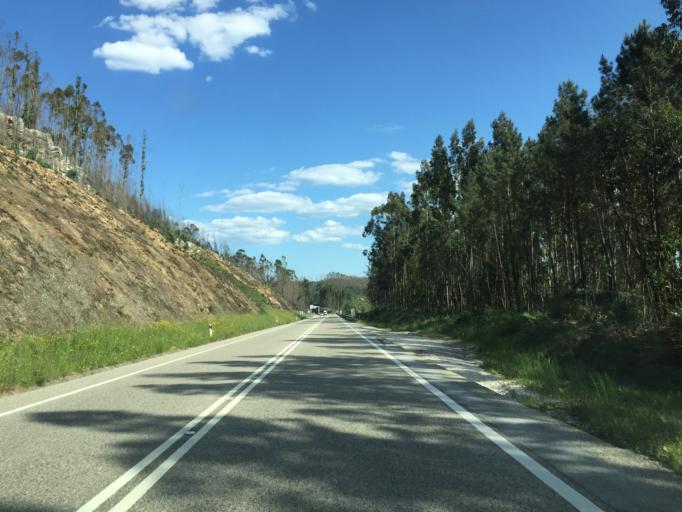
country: PT
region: Leiria
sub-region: Figueiro Dos Vinhos
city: Figueiro dos Vinhos
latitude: 39.9299
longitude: -8.3355
